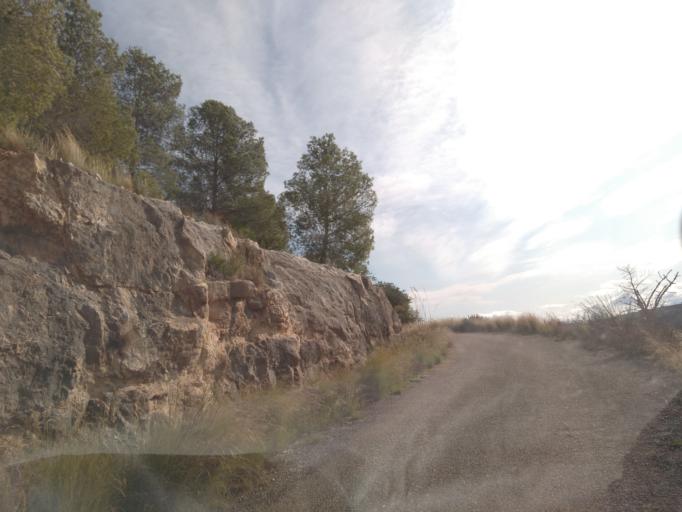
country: ES
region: Valencia
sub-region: Provincia de Valencia
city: Sumacarcer
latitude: 39.1527
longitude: -0.6556
